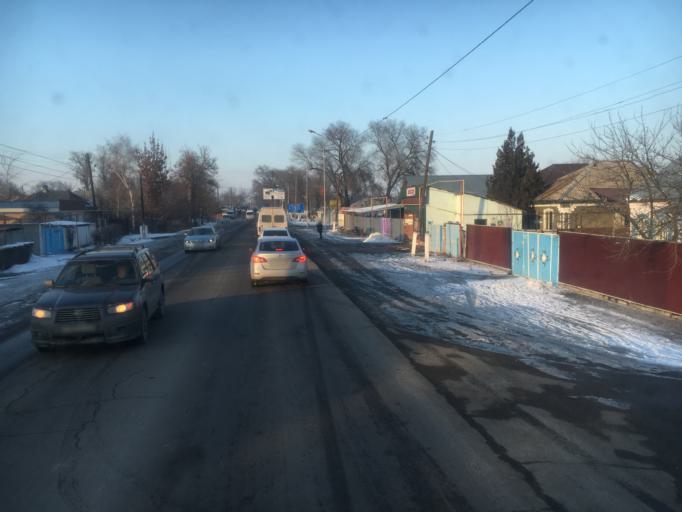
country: KZ
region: Almaty Oblysy
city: Burunday
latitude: 43.3736
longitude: 76.6418
